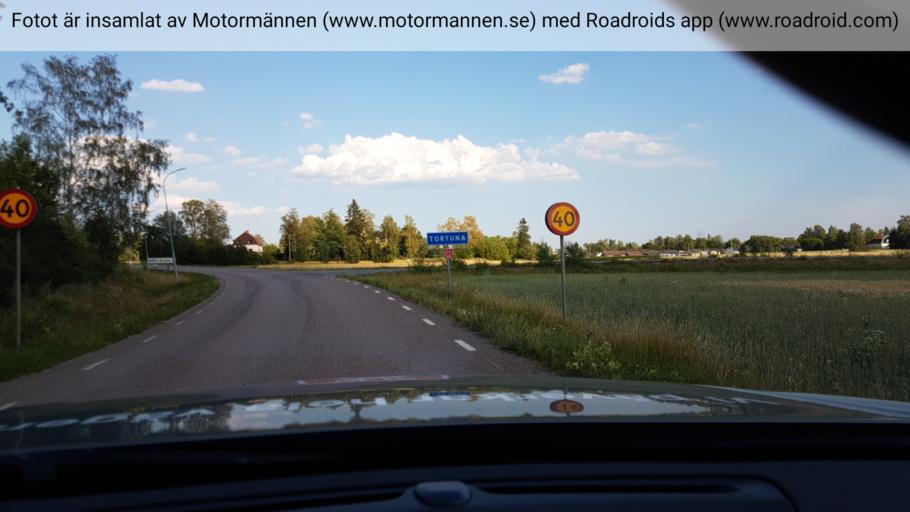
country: SE
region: Vaestmanland
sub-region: Vasteras
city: Tillberga
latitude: 59.6788
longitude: 16.7137
